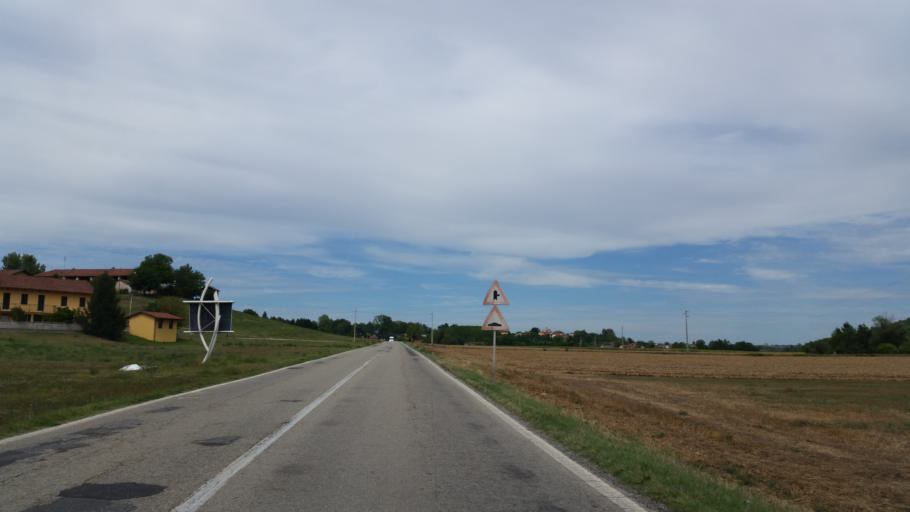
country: IT
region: Piedmont
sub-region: Provincia di Asti
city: Celle Enomondo
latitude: 44.8839
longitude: 8.1348
